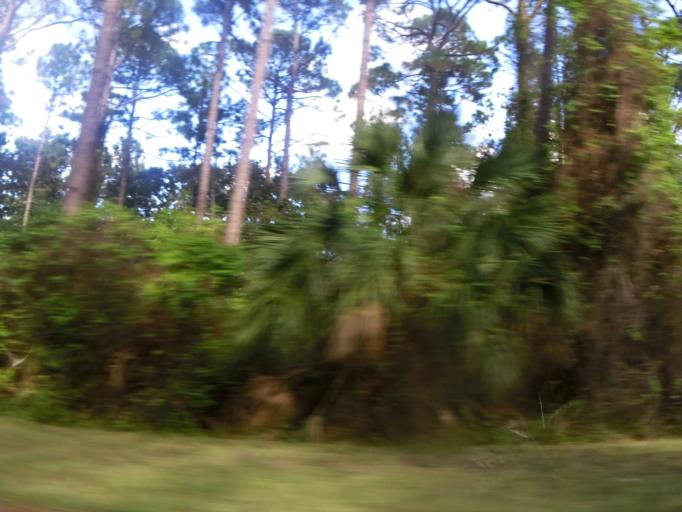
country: US
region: Florida
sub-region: Duval County
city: Atlantic Beach
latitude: 30.4831
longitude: -81.4393
